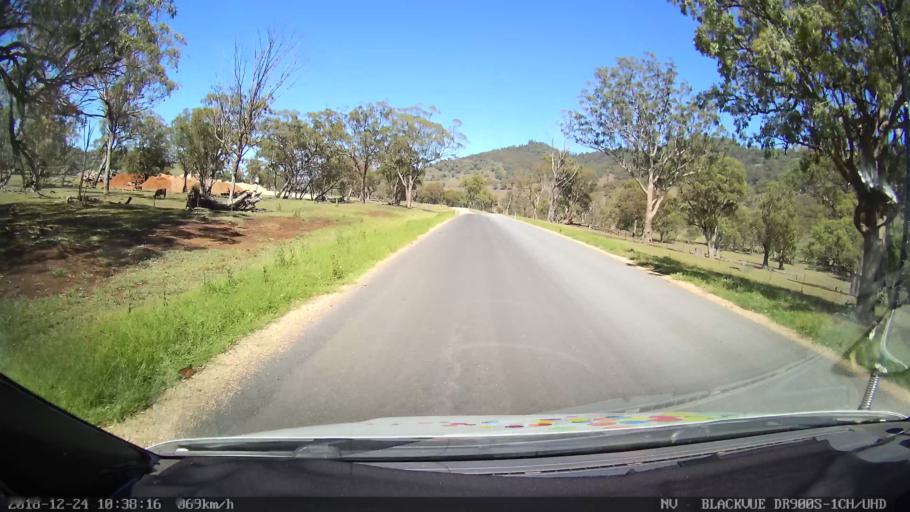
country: AU
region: New South Wales
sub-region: Upper Hunter Shire
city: Merriwa
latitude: -31.8481
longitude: 150.4838
